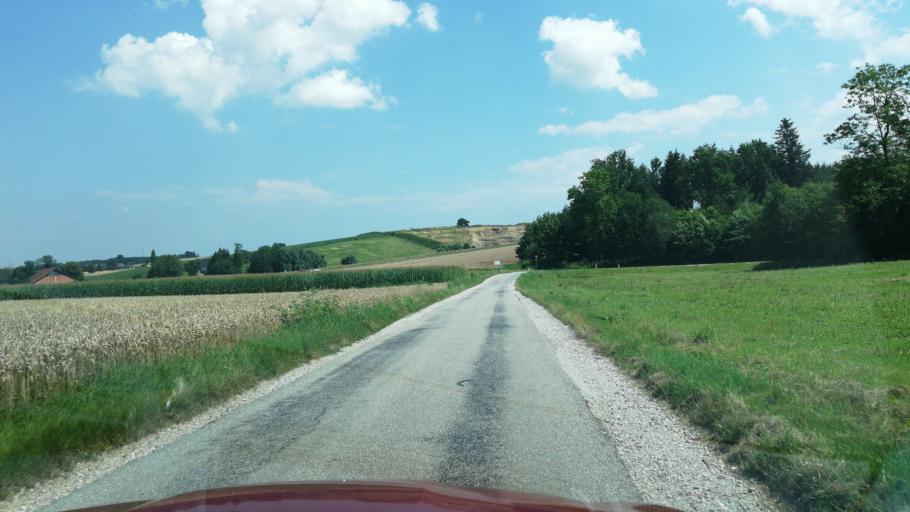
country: AT
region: Upper Austria
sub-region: Wels-Land
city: Buchkirchen
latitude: 48.2173
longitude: 14.0098
